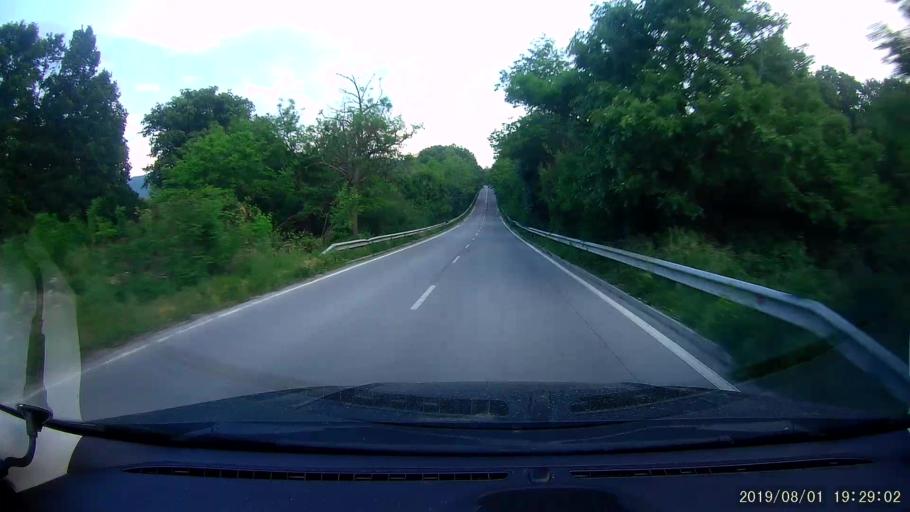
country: BG
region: Burgas
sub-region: Obshtina Sungurlare
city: Sungurlare
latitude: 42.8328
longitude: 26.9112
